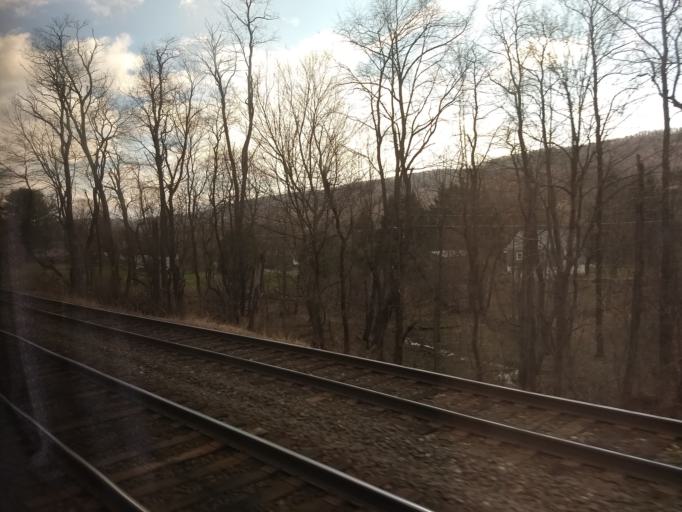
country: US
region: Pennsylvania
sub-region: Blair County
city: Tipton
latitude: 40.6445
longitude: -78.2787
